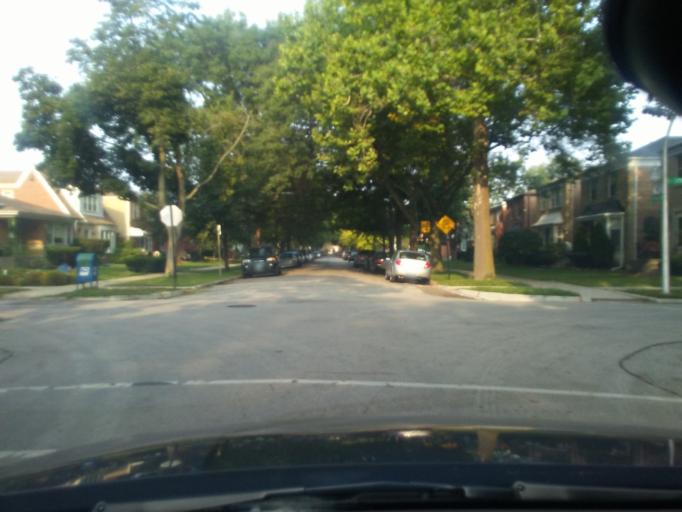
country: US
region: Illinois
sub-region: Cook County
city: Evanston
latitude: 42.0165
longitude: -87.7042
